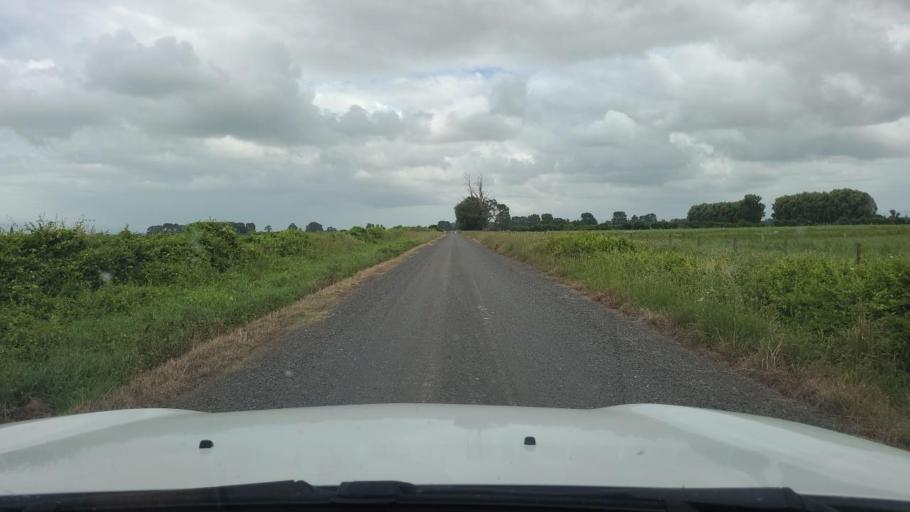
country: NZ
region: Bay of Plenty
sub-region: Western Bay of Plenty District
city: Katikati
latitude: -37.5853
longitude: 175.7131
